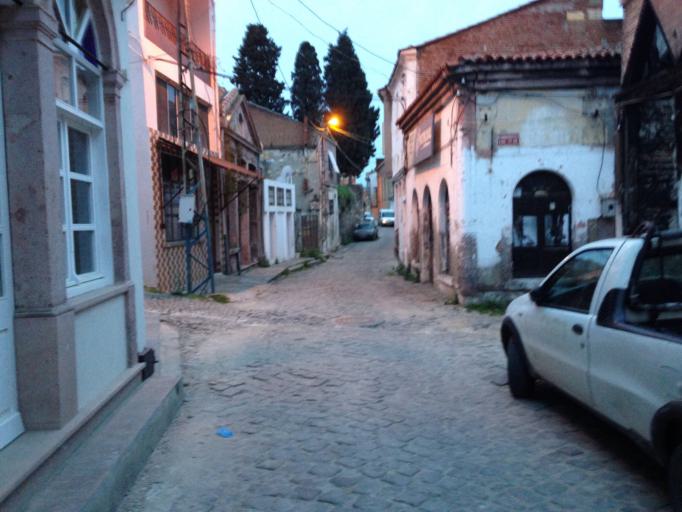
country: TR
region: Balikesir
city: Ayvalik
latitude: 39.3233
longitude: 26.6948
